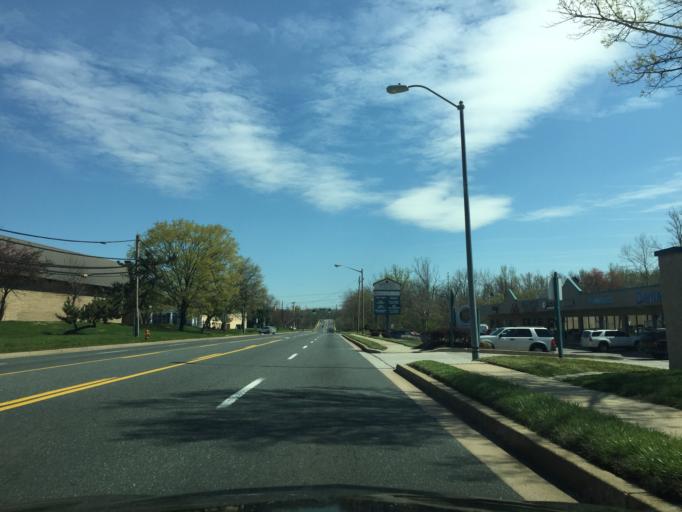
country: US
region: Maryland
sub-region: Baltimore County
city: Rossville
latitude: 39.3348
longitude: -76.4779
